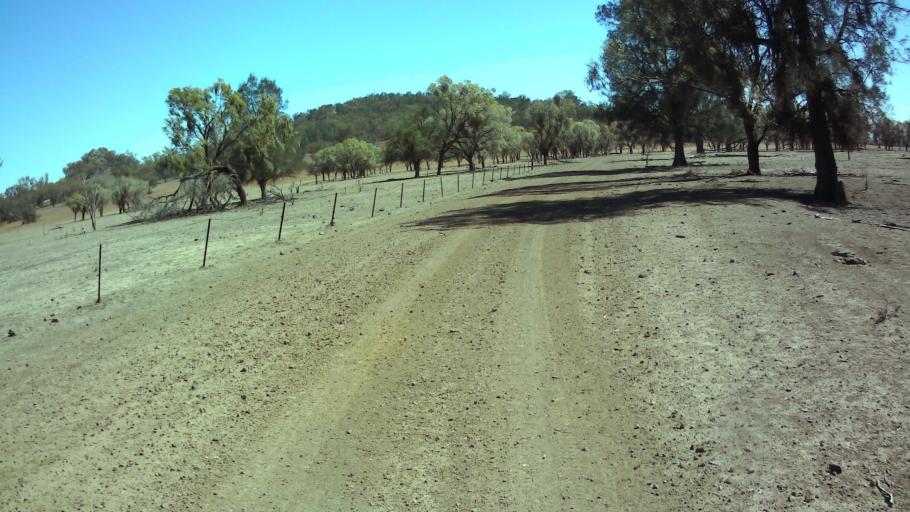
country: AU
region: New South Wales
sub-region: Forbes
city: Forbes
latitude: -33.7374
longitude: 147.6625
